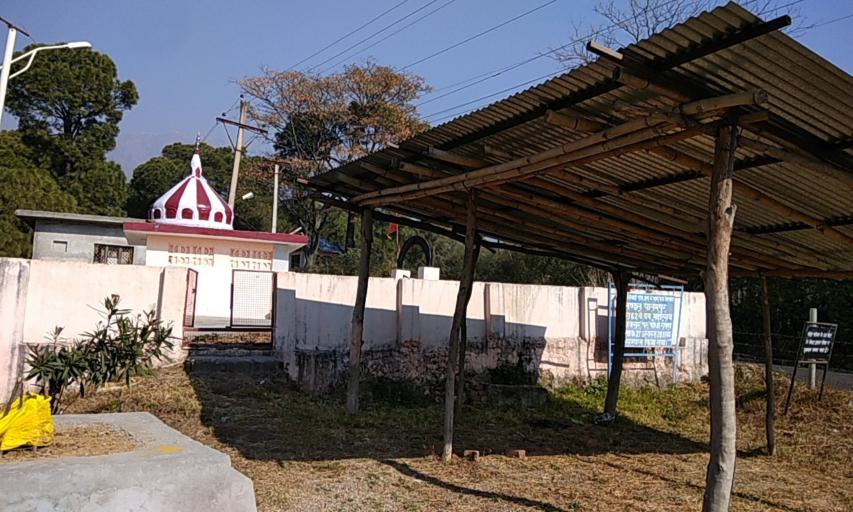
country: IN
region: Himachal Pradesh
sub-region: Kangra
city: Palampur
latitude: 32.1204
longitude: 76.5256
